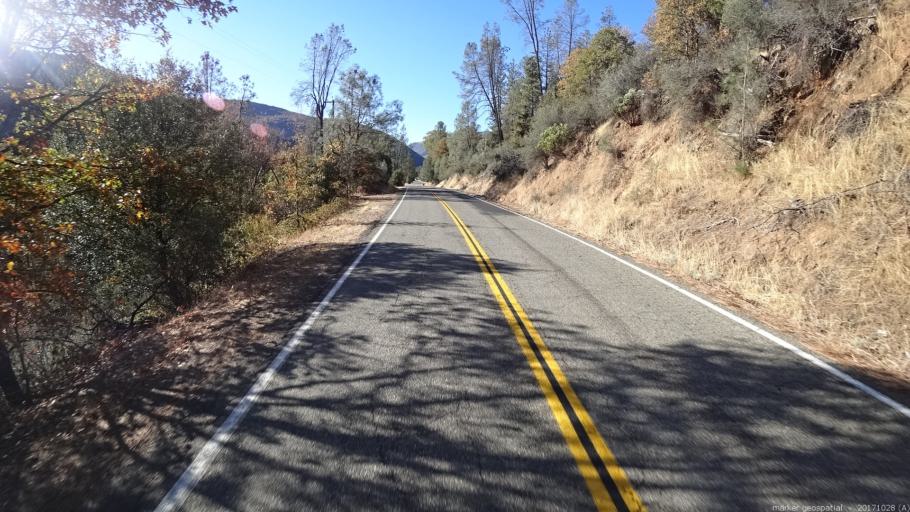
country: US
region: California
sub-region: Trinity County
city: Lewiston
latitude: 40.7258
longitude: -122.6255
